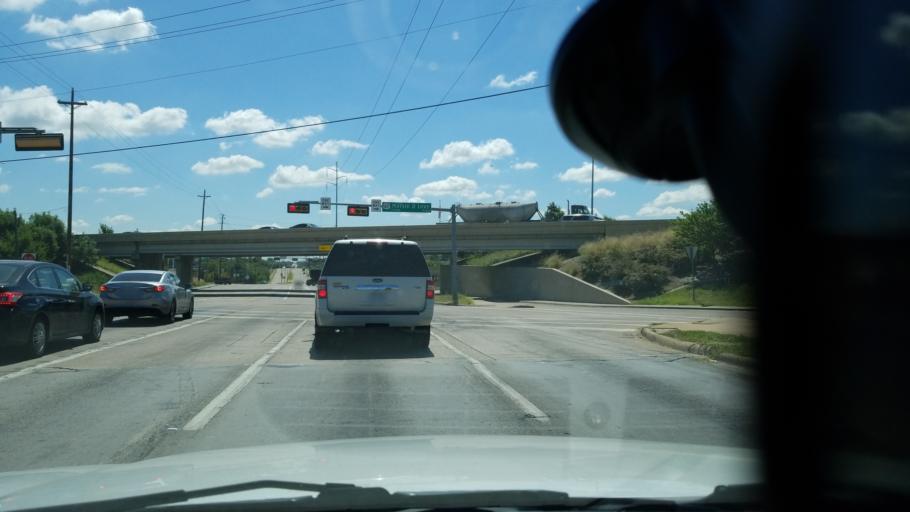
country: US
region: Texas
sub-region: Dallas County
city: Duncanville
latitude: 32.6621
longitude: -96.8711
